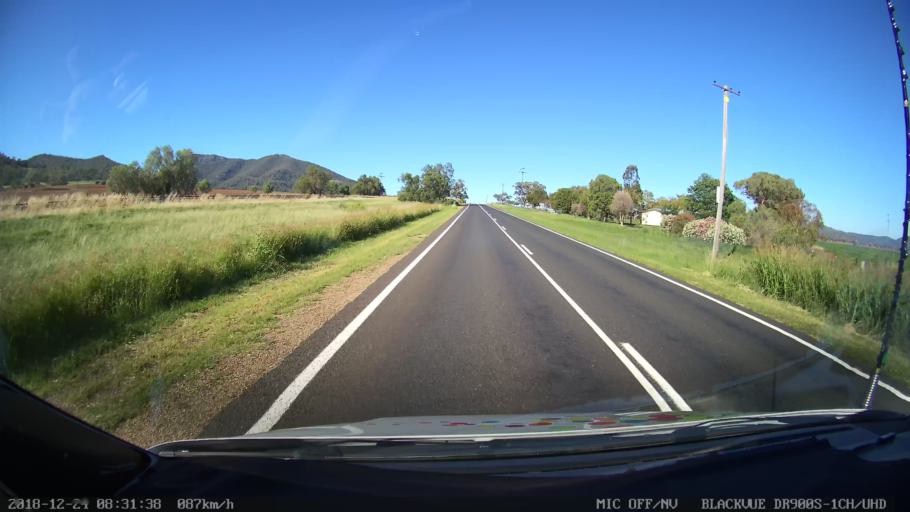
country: AU
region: New South Wales
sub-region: Tamworth Municipality
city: Phillip
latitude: -31.2748
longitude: 150.7088
